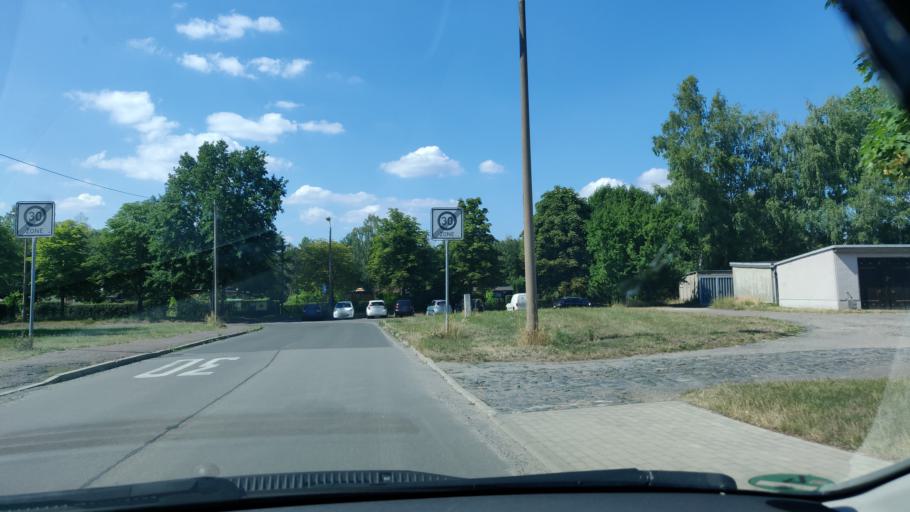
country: DE
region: Saxony
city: Borna
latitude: 51.1348
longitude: 12.4897
